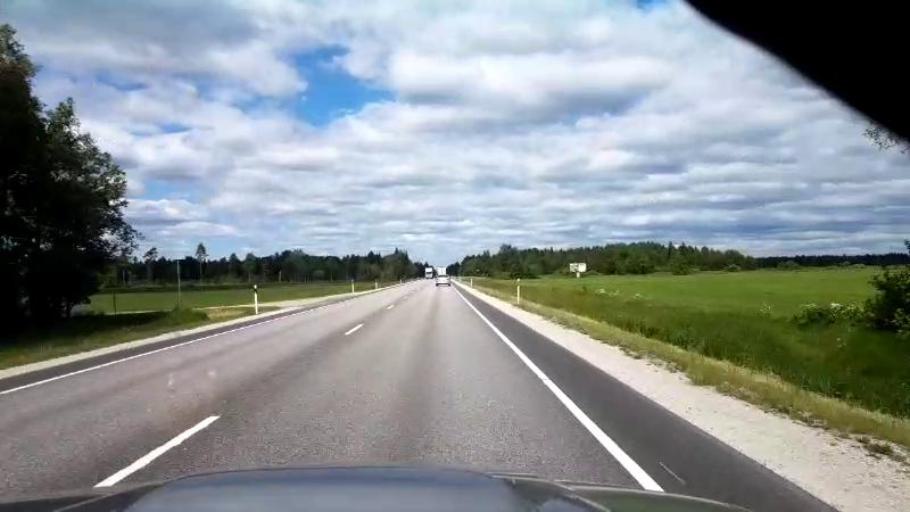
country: EE
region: Paernumaa
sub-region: Halinga vald
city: Parnu-Jaagupi
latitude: 58.7360
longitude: 24.4235
